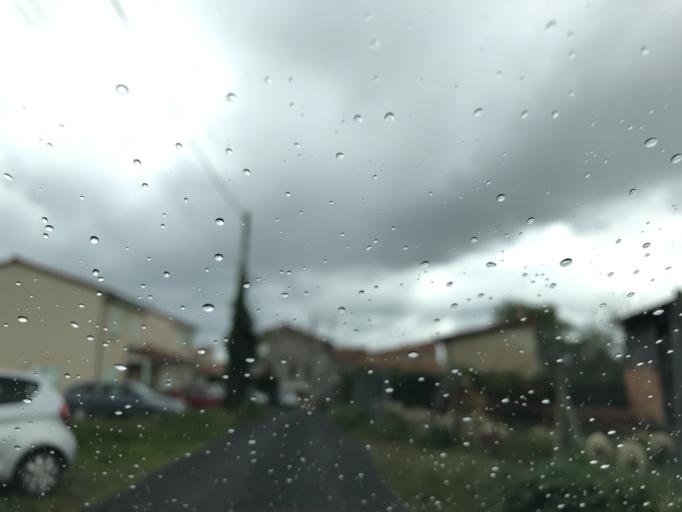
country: FR
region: Auvergne
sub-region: Departement du Puy-de-Dome
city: Billom
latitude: 45.7496
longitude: 3.3375
